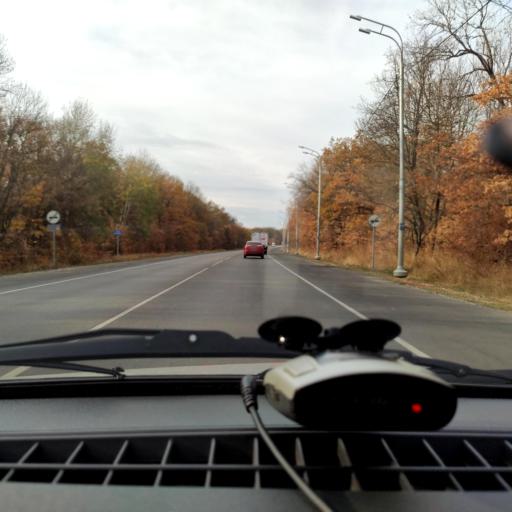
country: RU
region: Voronezj
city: Semiluki
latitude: 51.6374
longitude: 39.0061
